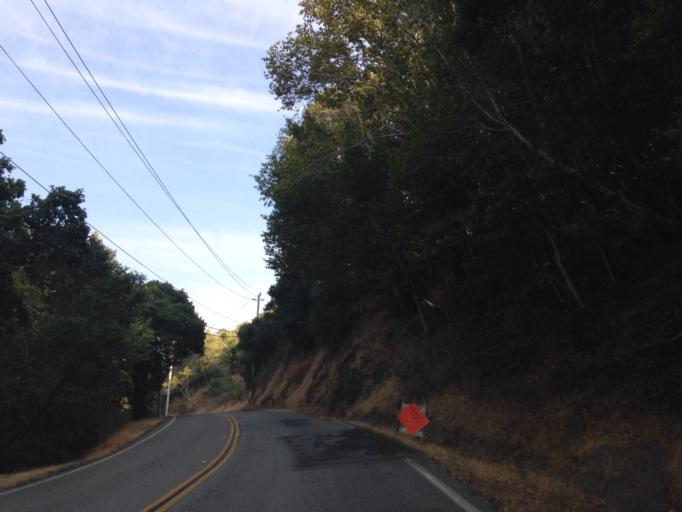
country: US
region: California
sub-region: Marin County
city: Lucas Valley-Marinwood
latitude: 38.0384
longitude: -122.6017
